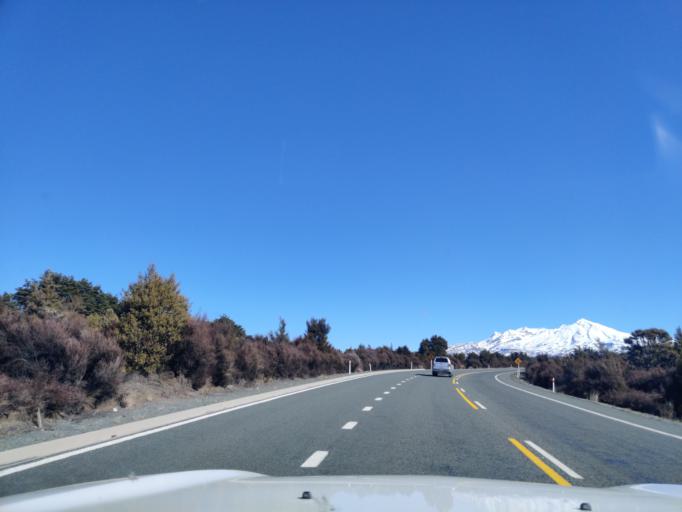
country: NZ
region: Waikato
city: Turangi
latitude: -39.2086
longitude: 175.7501
